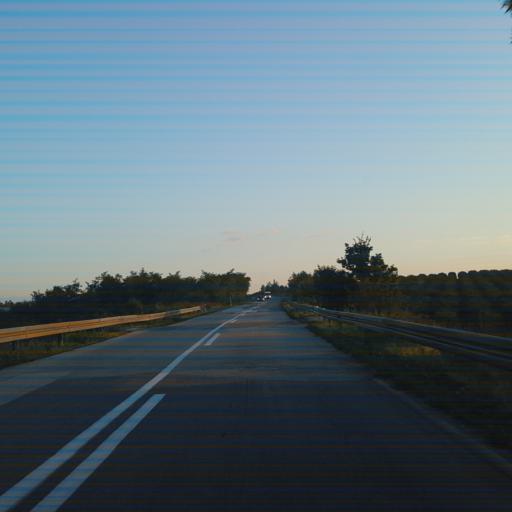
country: RS
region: Central Serbia
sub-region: Zajecarski Okrug
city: Zajecar
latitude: 44.0027
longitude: 22.3018
